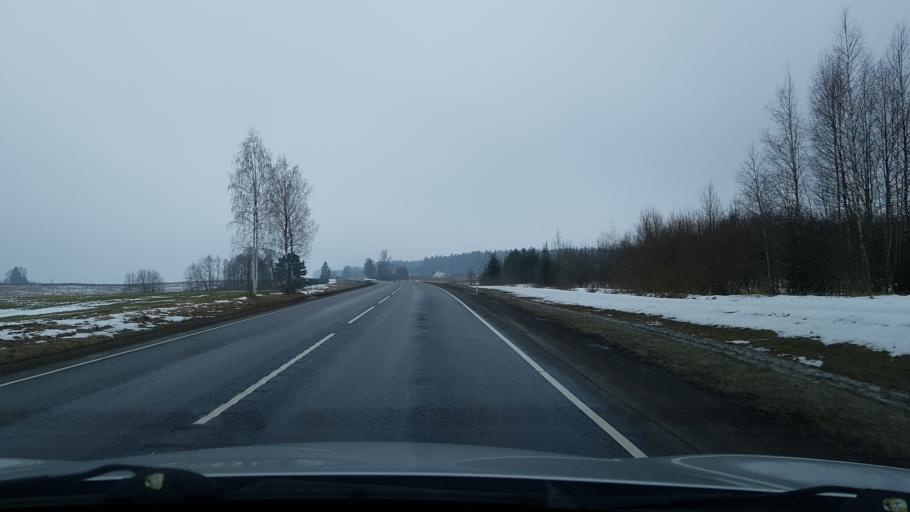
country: EE
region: Valgamaa
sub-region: Valga linn
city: Valga
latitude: 57.8448
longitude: 26.1281
